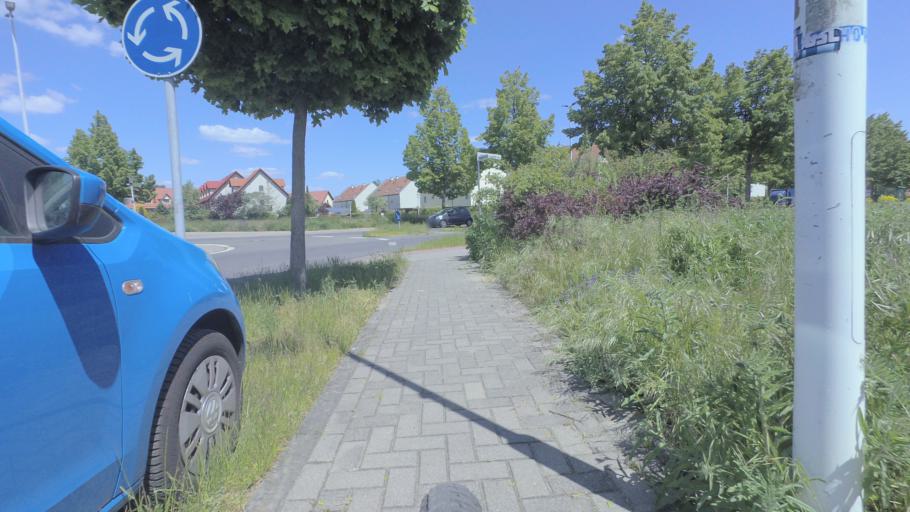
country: DE
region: Brandenburg
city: Rangsdorf
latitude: 52.3380
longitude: 13.3953
